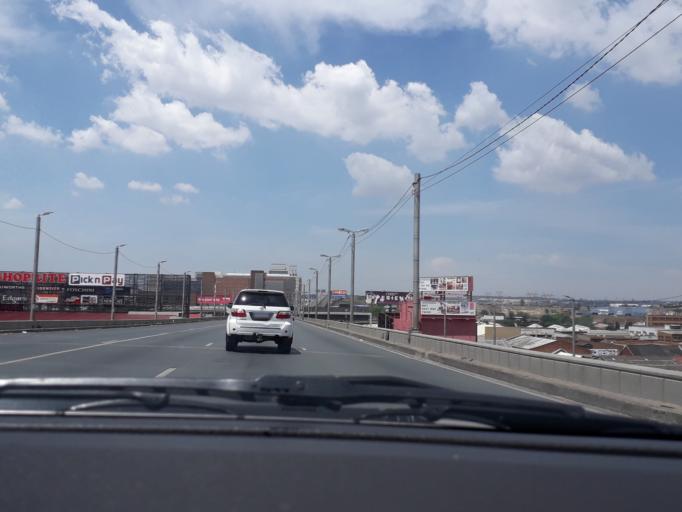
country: ZA
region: Gauteng
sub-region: City of Johannesburg Metropolitan Municipality
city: Johannesburg
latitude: -26.2002
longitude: 28.0301
